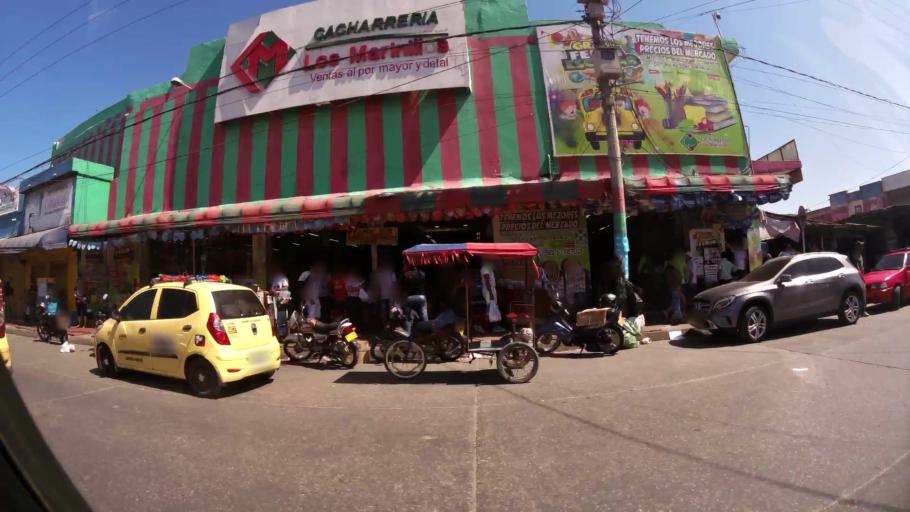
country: CO
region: Atlantico
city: Barranquilla
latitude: 10.9786
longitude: -74.7758
